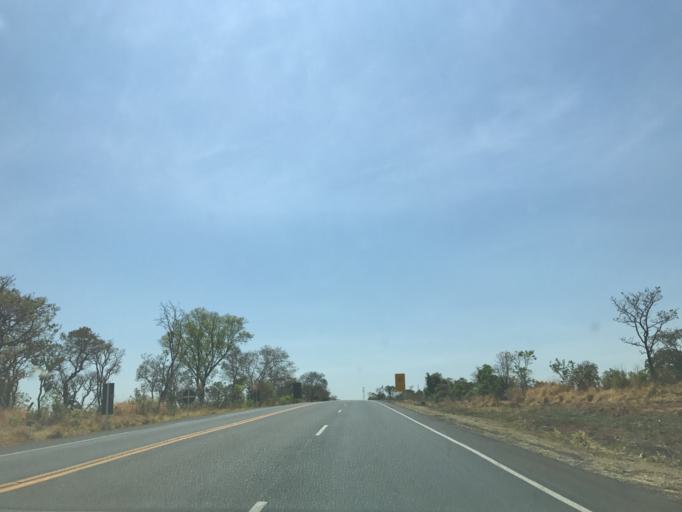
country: BR
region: Minas Gerais
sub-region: Frutal
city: Frutal
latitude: -19.8662
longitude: -48.9686
